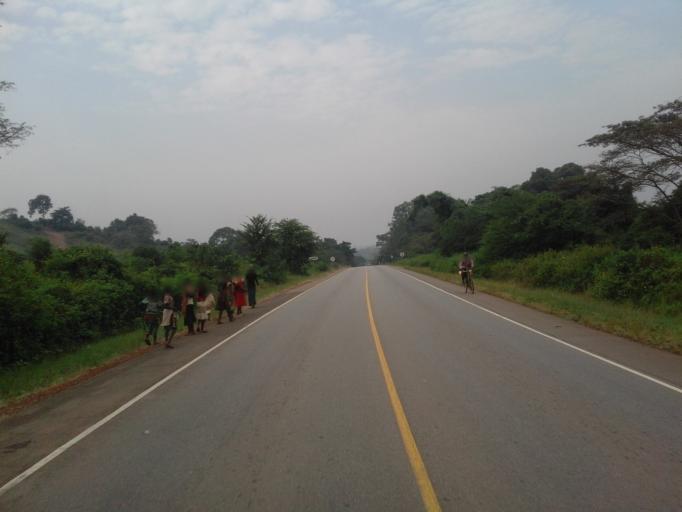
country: UG
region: Eastern Region
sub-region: Busia District
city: Busia
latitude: 0.5451
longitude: 34.0159
